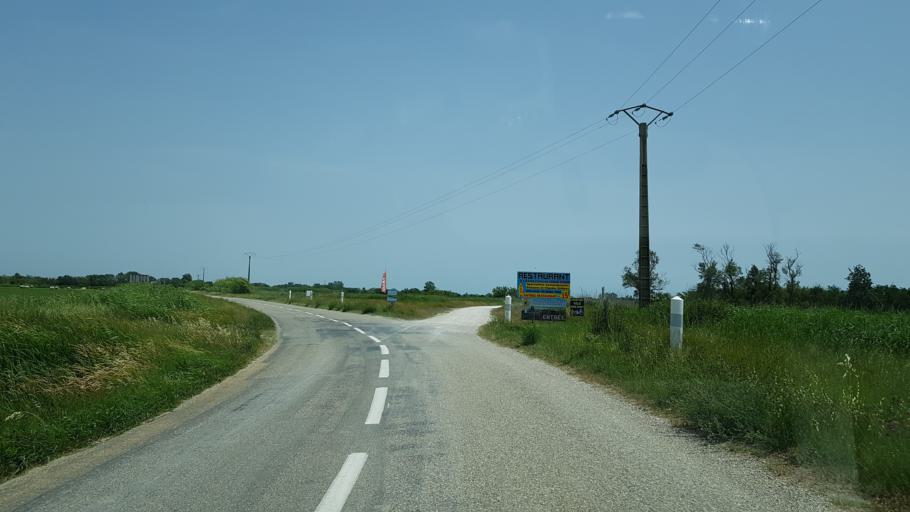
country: FR
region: Provence-Alpes-Cote d'Azur
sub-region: Departement des Bouches-du-Rhone
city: Port-Saint-Louis-du-Rhone
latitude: 43.4446
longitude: 4.6676
